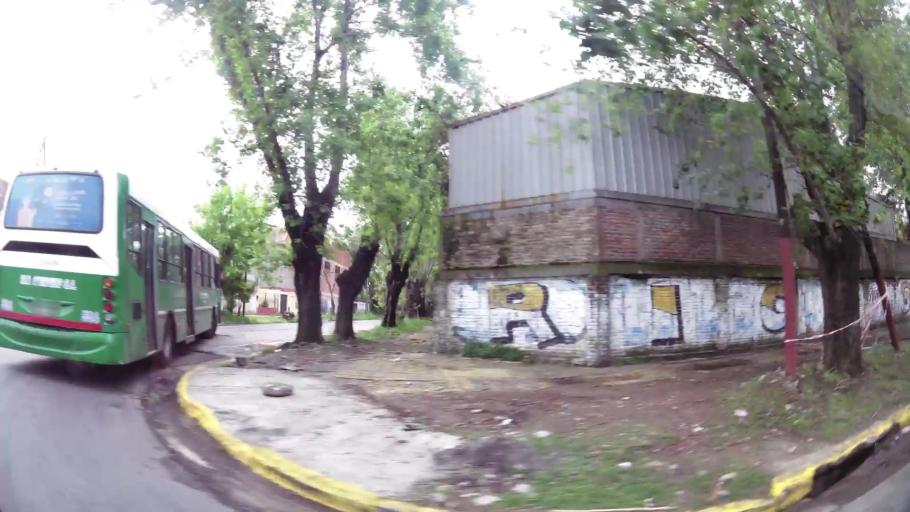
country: AR
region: Buenos Aires
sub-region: Partido de Lanus
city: Lanus
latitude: -34.7073
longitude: -58.3639
